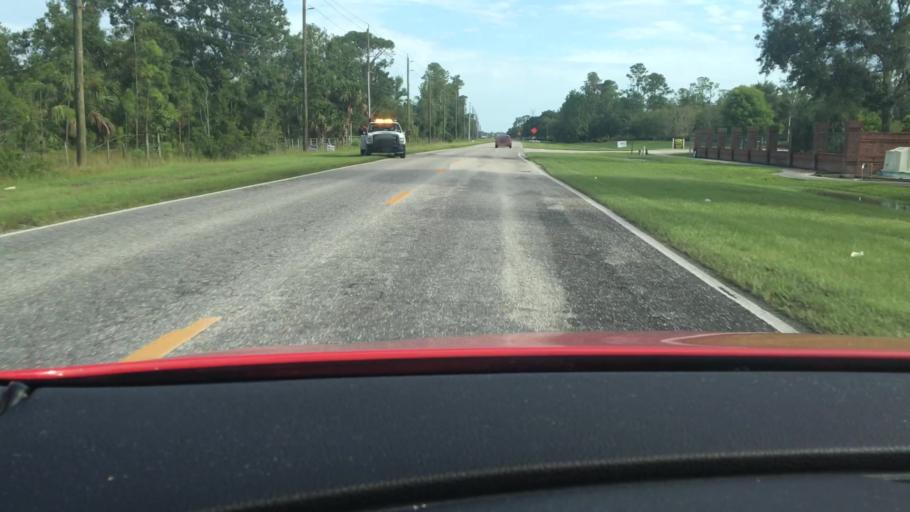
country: US
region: Florida
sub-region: Volusia County
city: Daytona Beach
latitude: 29.1756
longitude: -81.0902
